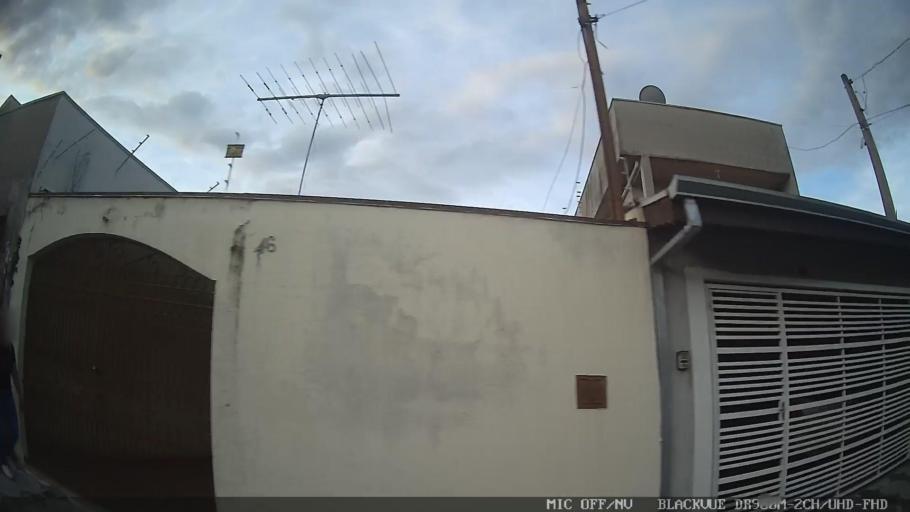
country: BR
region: Sao Paulo
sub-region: Mogi das Cruzes
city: Mogi das Cruzes
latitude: -23.5188
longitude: -46.1959
